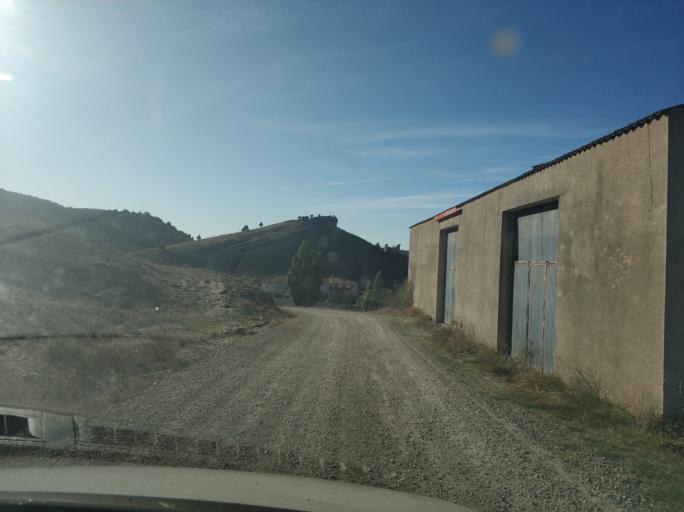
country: ES
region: Castille and Leon
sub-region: Provincia de Burgos
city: Hontoria del Pinar
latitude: 41.8435
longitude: -3.1633
